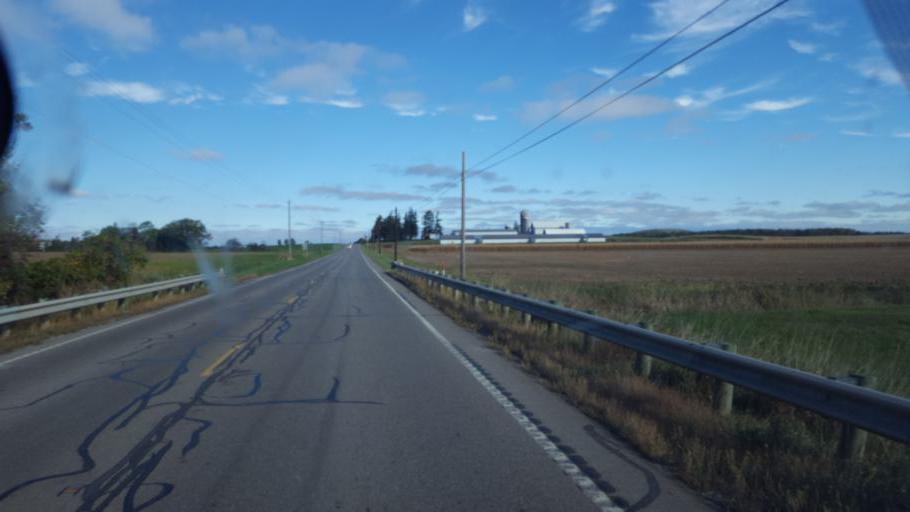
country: US
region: Ohio
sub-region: Huron County
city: Greenwich
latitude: 40.9469
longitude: -82.4948
